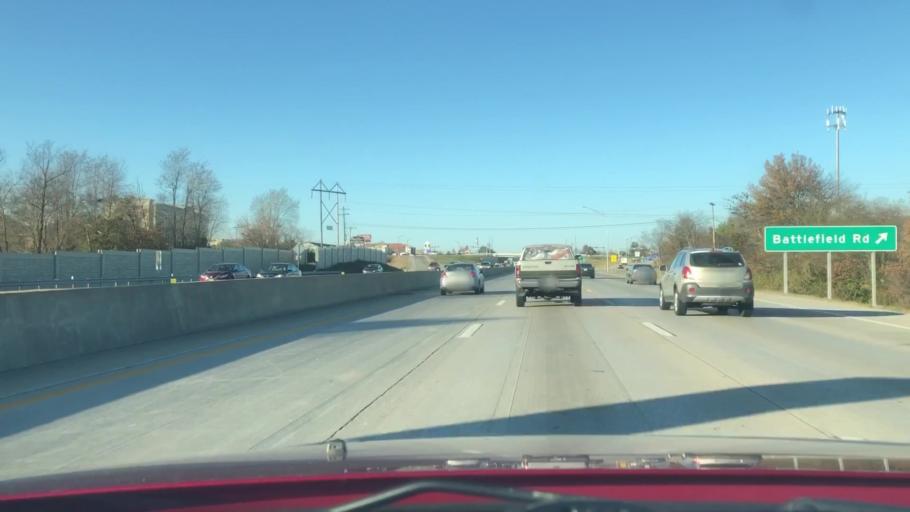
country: US
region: Missouri
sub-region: Greene County
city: Springfield
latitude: 37.1530
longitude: -93.2244
